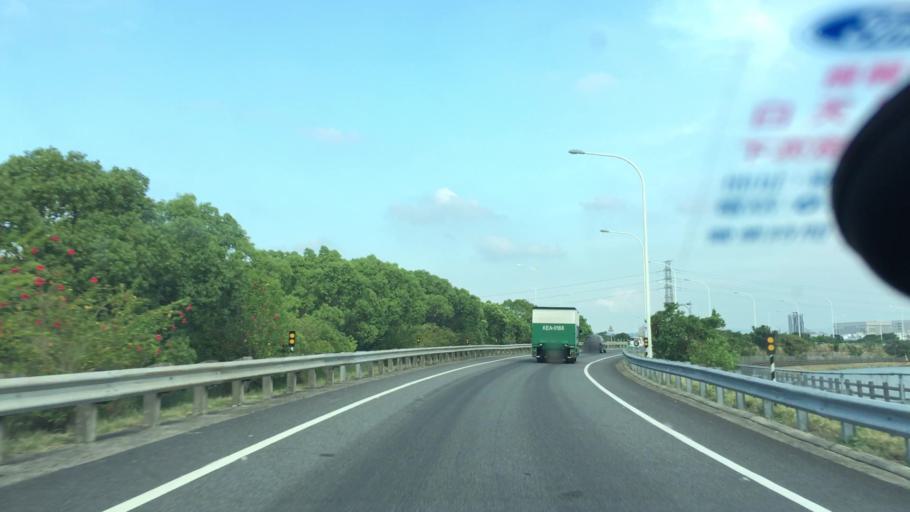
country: TW
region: Taiwan
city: Taoyuan City
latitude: 25.0163
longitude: 121.2741
